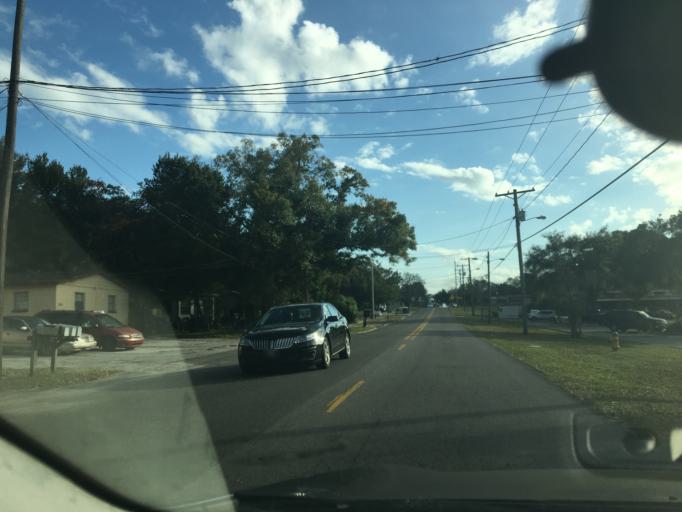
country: US
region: Florida
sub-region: Hillsborough County
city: Temple Terrace
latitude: 28.0308
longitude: -82.4100
